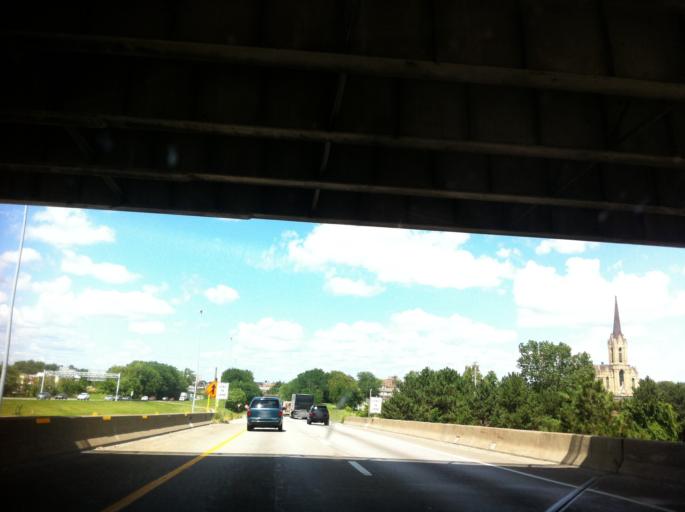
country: US
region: Ohio
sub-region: Lucas County
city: Toledo
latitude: 41.6455
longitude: -83.5486
